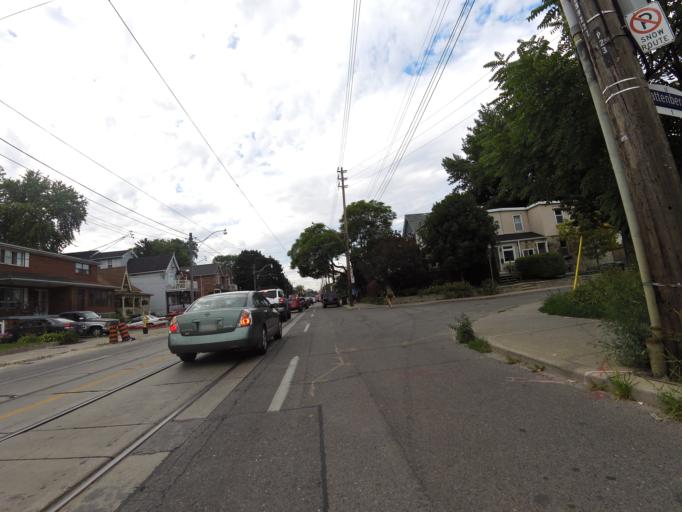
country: CA
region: Ontario
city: Toronto
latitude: 43.6670
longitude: -79.3168
